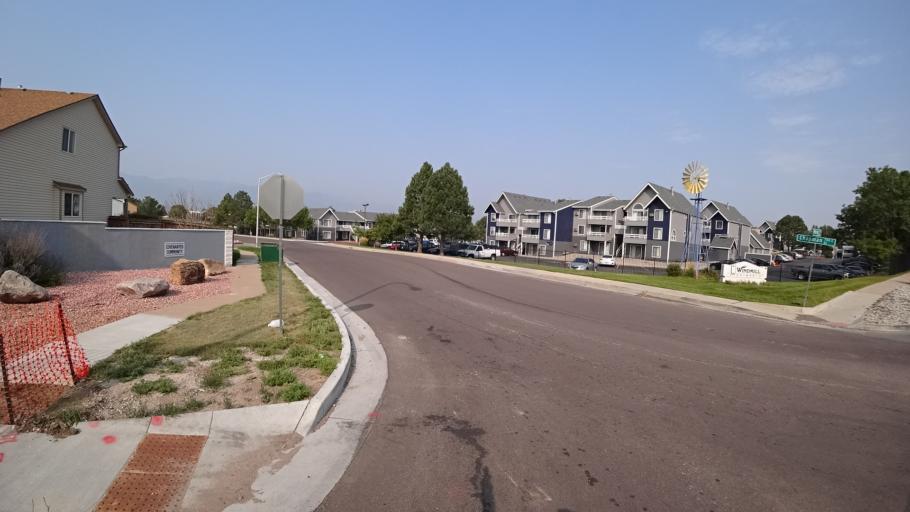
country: US
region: Colorado
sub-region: El Paso County
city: Stratmoor
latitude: 38.8217
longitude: -104.7505
